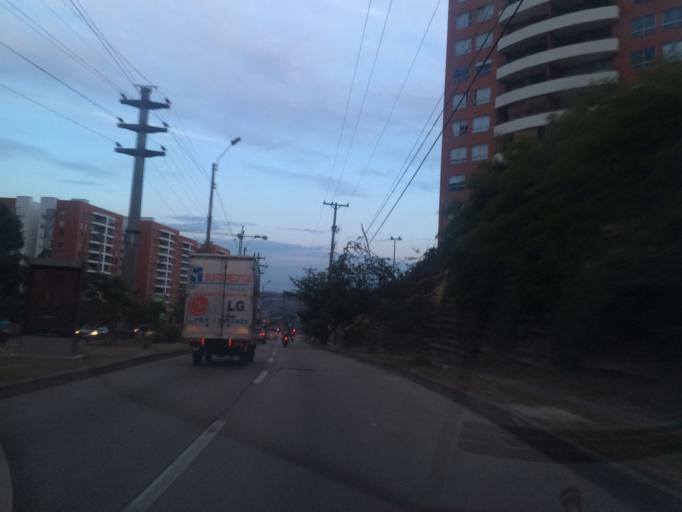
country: CO
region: Valle del Cauca
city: Cali
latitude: 3.4322
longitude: -76.5511
